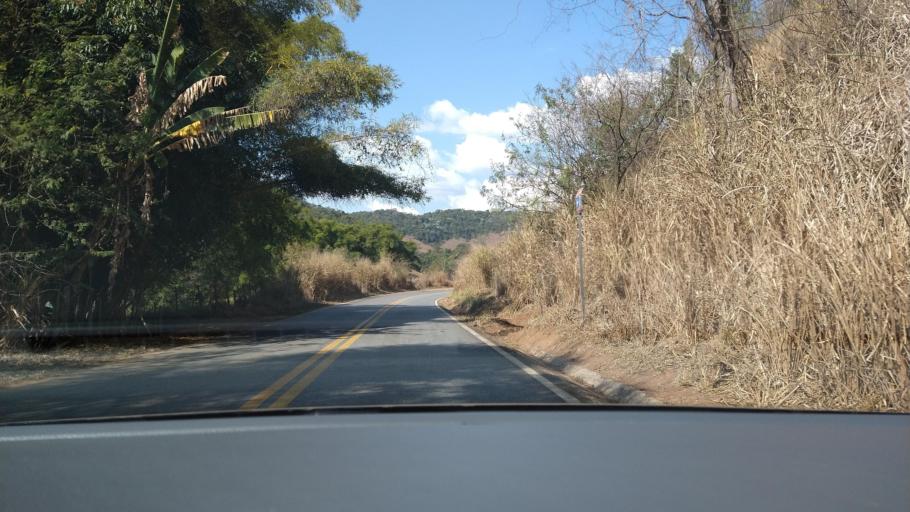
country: BR
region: Minas Gerais
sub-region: Rio Piracicaba
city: Rio Piracicaba
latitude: -19.9552
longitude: -43.1631
